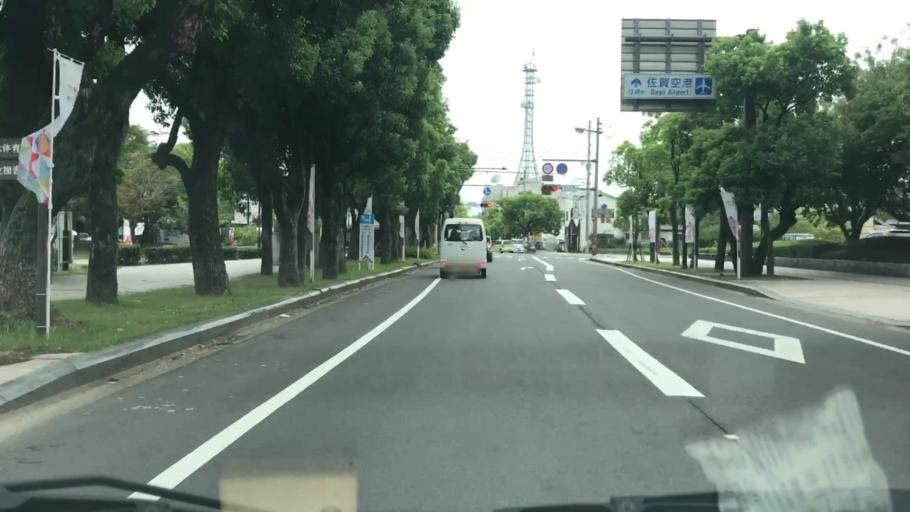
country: JP
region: Saga Prefecture
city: Saga-shi
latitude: 33.2496
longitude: 130.3004
